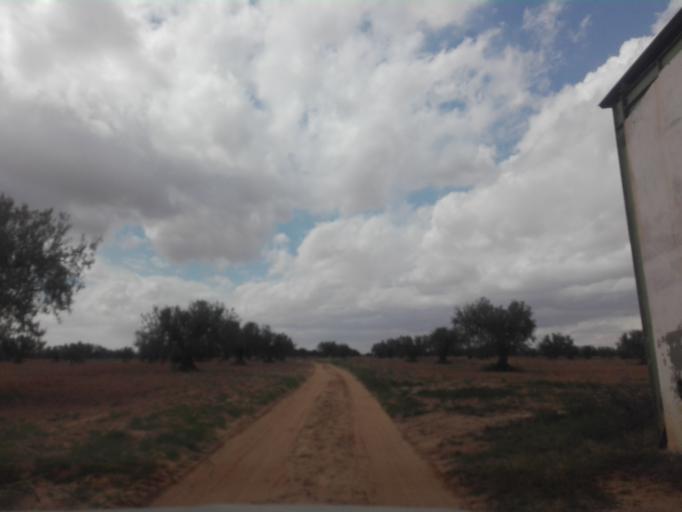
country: TN
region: Safaqis
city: Sfax
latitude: 34.6918
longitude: 10.4503
